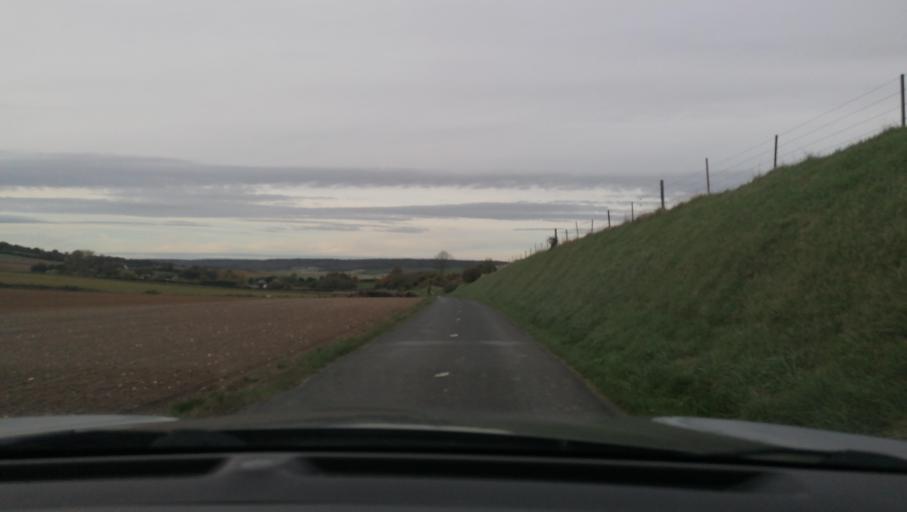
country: FR
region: Picardie
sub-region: Departement de la Somme
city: Bouttencourt
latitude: 49.8971
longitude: 1.6743
